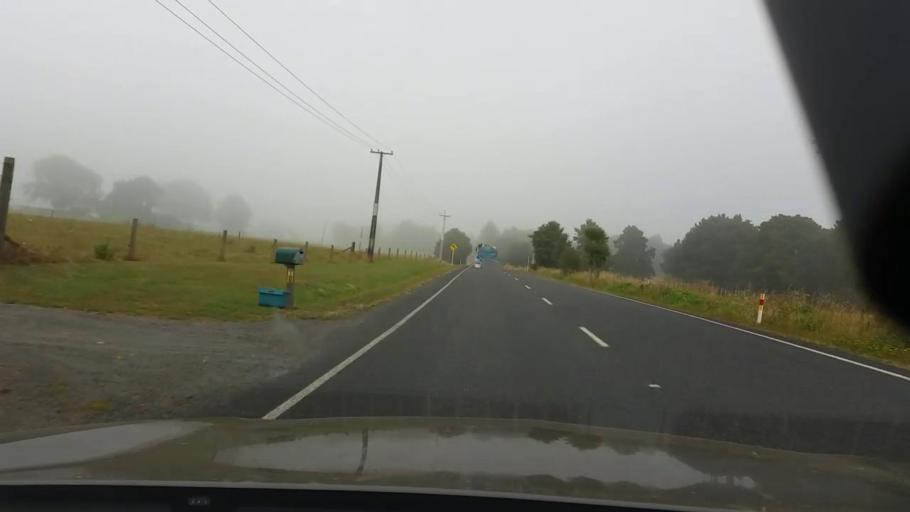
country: NZ
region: Waikato
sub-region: Waikato District
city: Ngaruawahia
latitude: -37.6381
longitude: 175.2969
